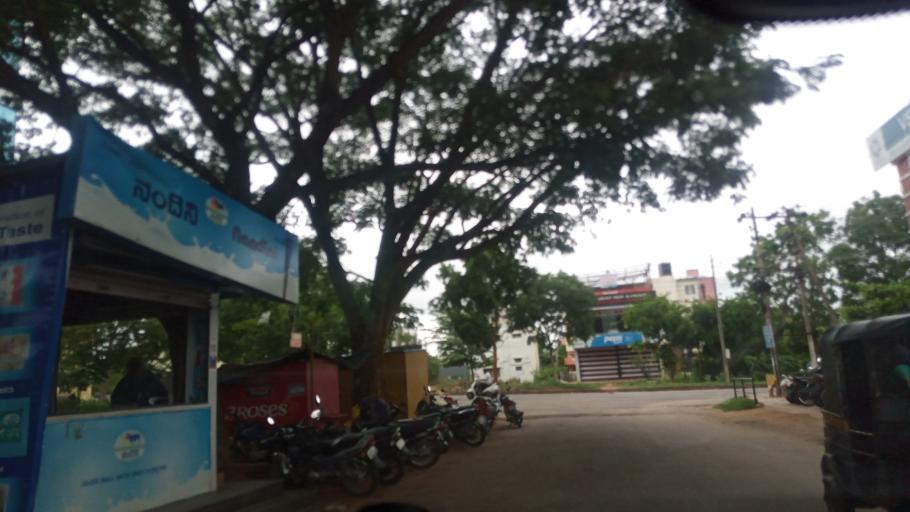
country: IN
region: Karnataka
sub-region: Mysore
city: Mysore
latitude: 12.2861
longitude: 76.6127
